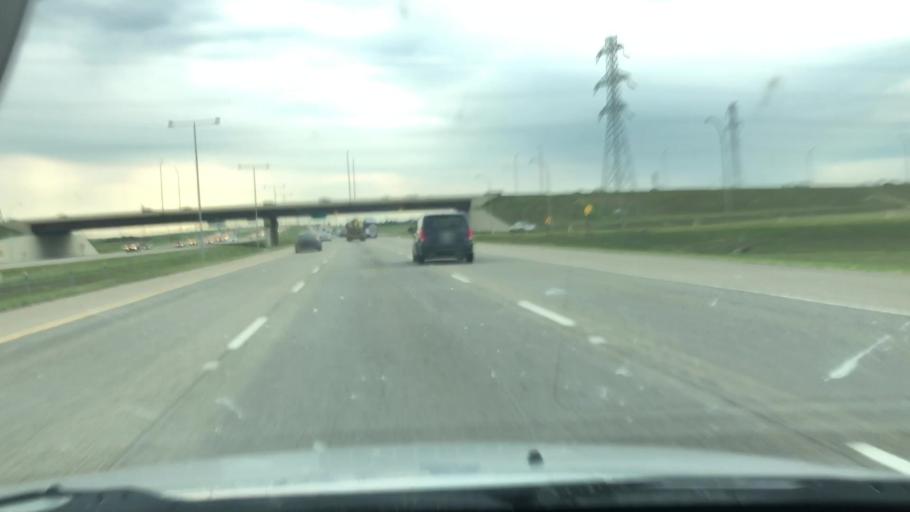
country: CA
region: Alberta
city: Beaumont
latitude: 53.4375
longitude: -113.4632
